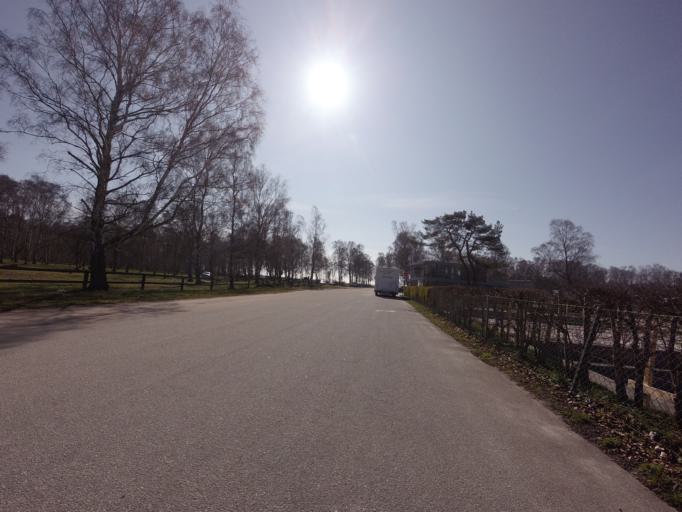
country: SE
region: Skane
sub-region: Vellinge Kommun
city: Skanor med Falsterbo
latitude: 55.3981
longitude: 12.8652
